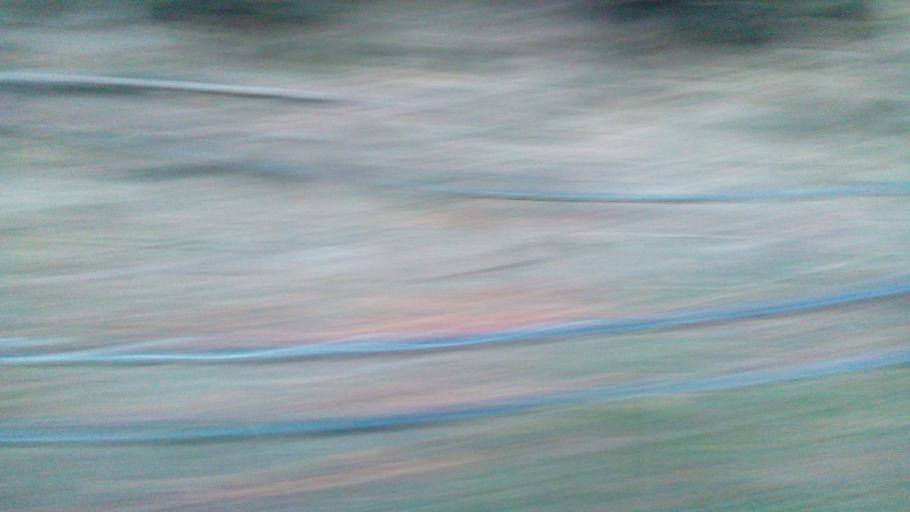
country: TW
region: Taiwan
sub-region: Hualien
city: Hualian
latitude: 24.3475
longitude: 121.3180
